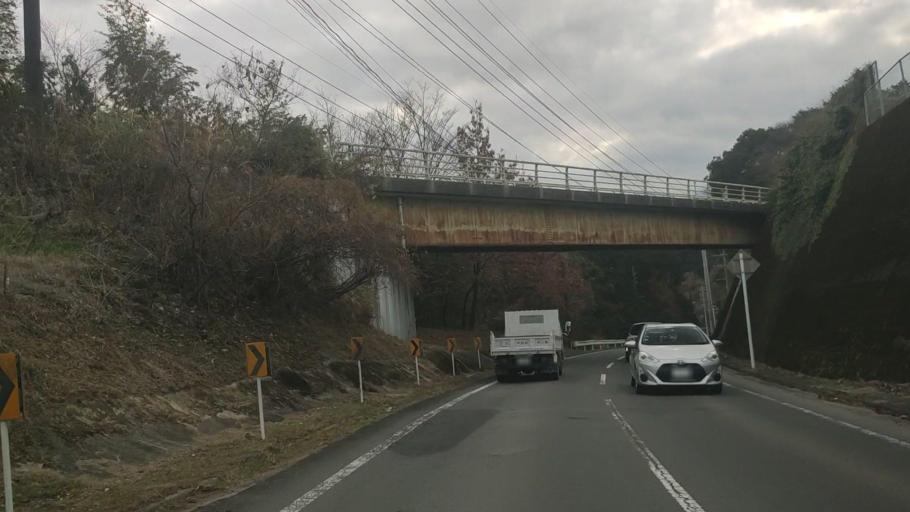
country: JP
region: Nagasaki
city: Shimabara
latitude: 32.8523
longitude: 130.2750
